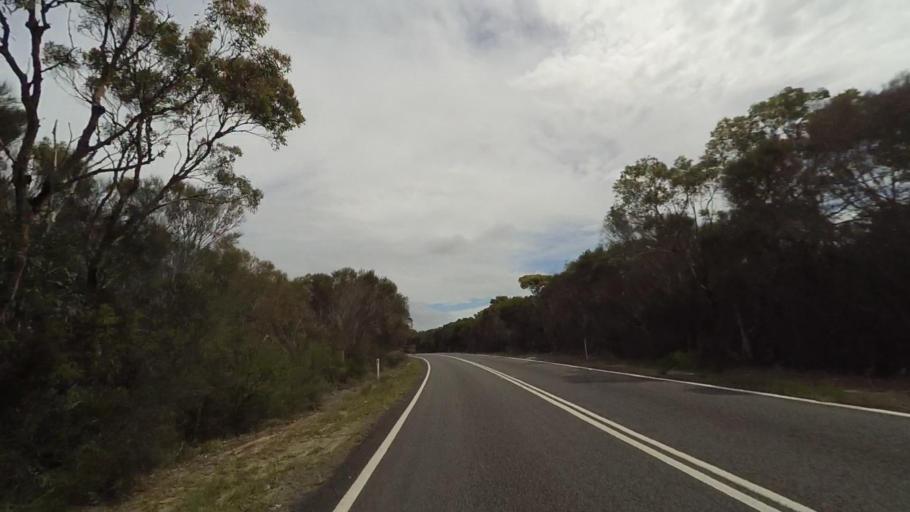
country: AU
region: New South Wales
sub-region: Sutherland Shire
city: Bundeena
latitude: -34.0965
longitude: 151.1251
